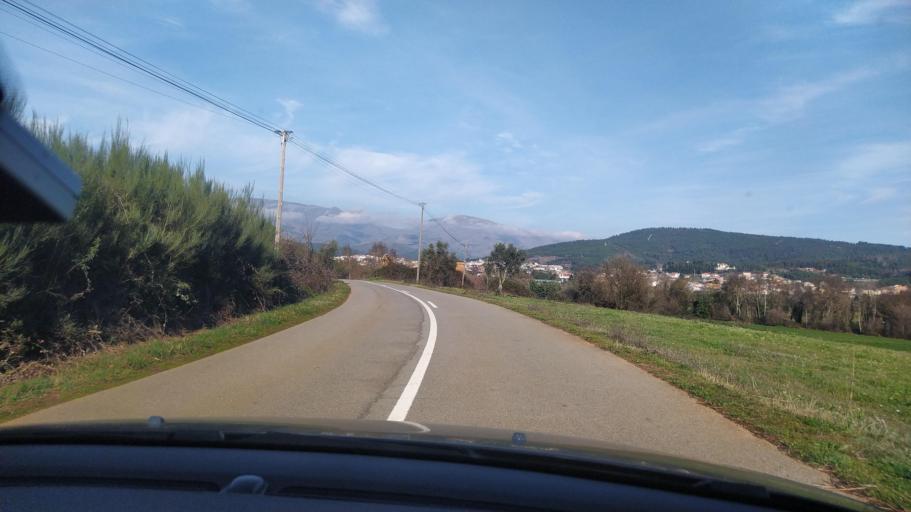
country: PT
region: Castelo Branco
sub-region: Concelho do Fundao
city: Aldeia de Joanes
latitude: 40.1848
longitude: -7.6443
